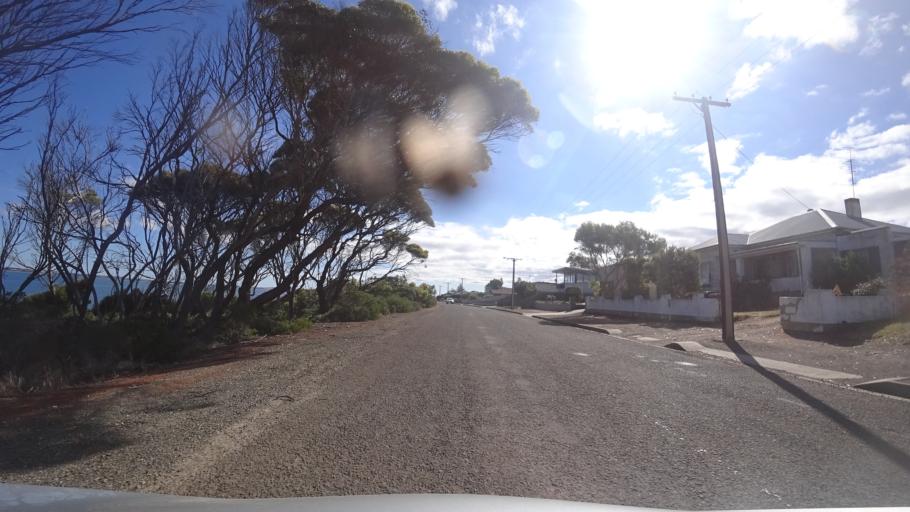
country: AU
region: South Australia
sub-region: Kangaroo Island
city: Kingscote
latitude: -35.6582
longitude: 137.6373
